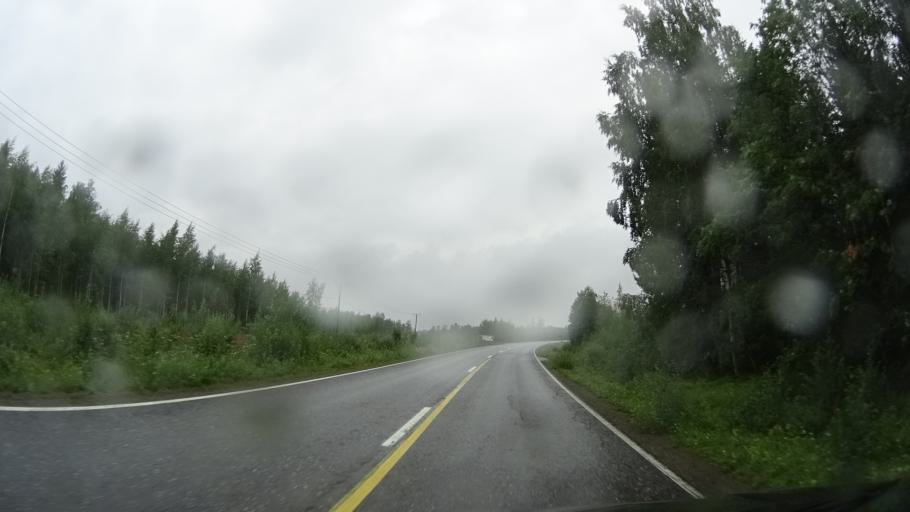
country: FI
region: North Karelia
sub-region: Keski-Karjala
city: Raeaekkylae
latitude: 62.3109
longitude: 29.5210
